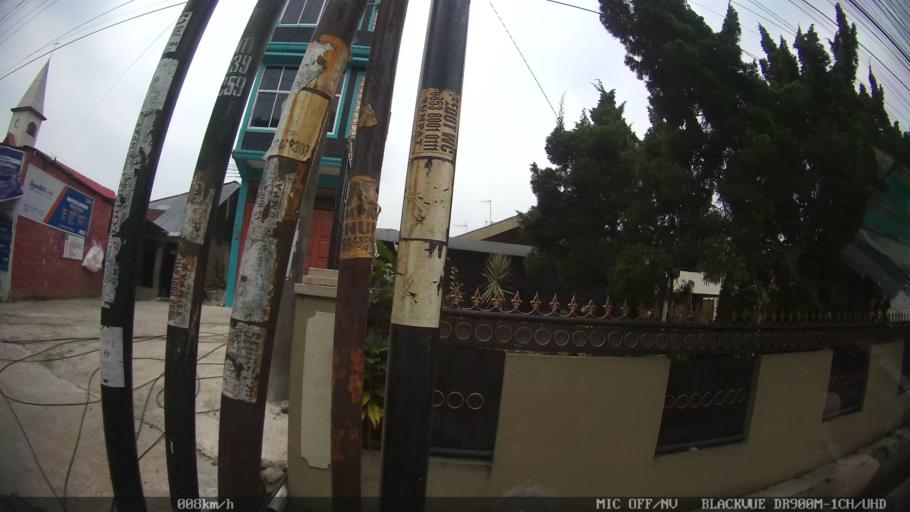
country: ID
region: North Sumatra
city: Medan
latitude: 3.5657
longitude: 98.7022
